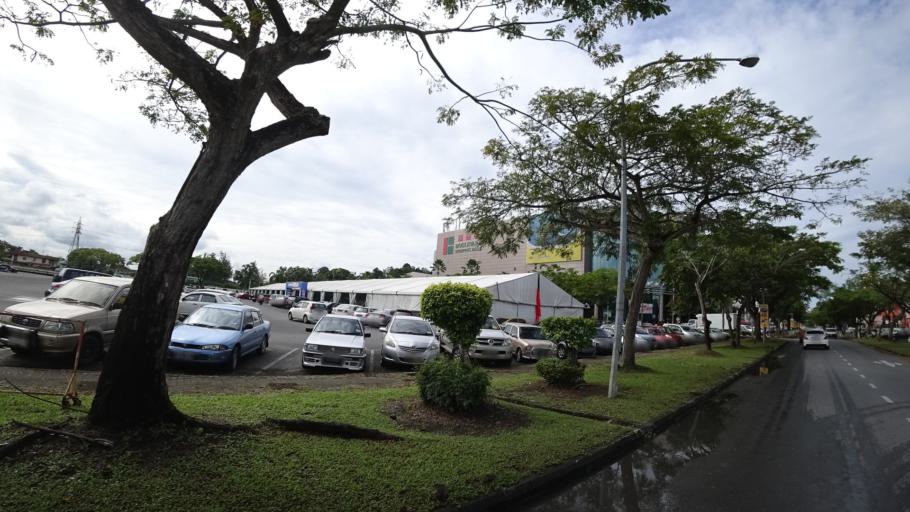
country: MY
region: Sarawak
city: Miri
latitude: 4.4163
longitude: 114.0132
